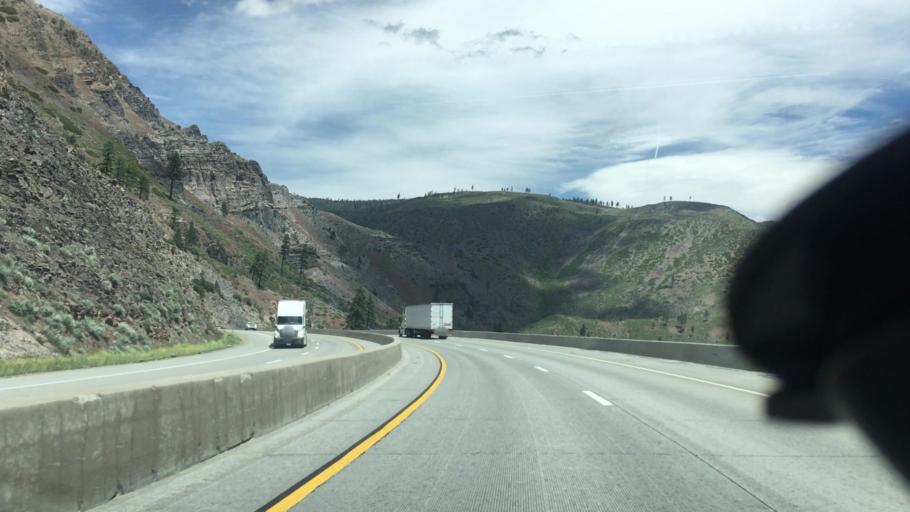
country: US
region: California
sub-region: Placer County
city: Tahoe Vista
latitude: 39.3732
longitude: -120.0330
